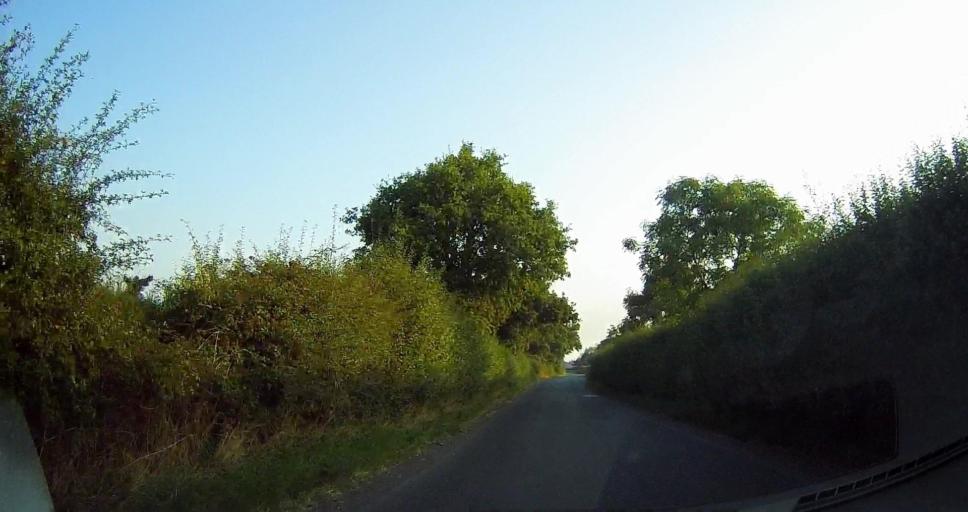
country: GB
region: England
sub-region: Cheshire East
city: Nantwich
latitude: 53.0319
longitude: -2.5178
